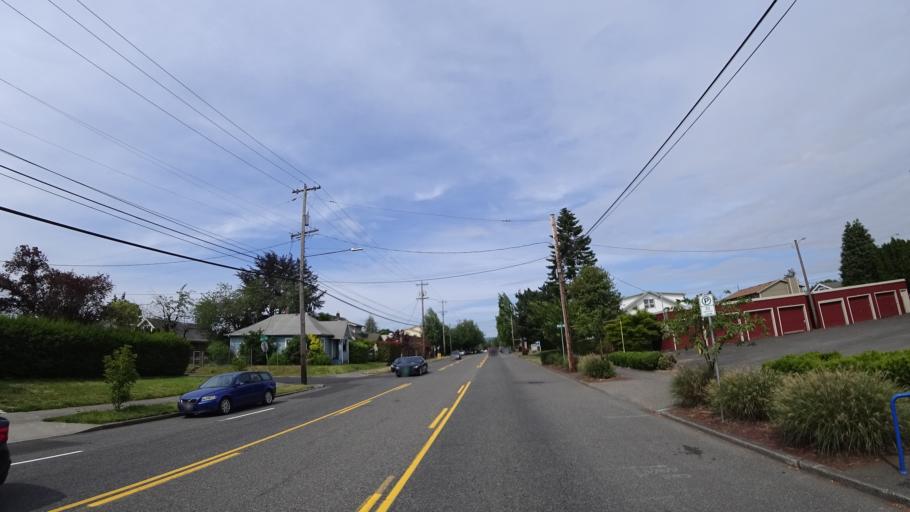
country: US
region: Oregon
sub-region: Multnomah County
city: Lents
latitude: 45.5265
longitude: -122.6051
